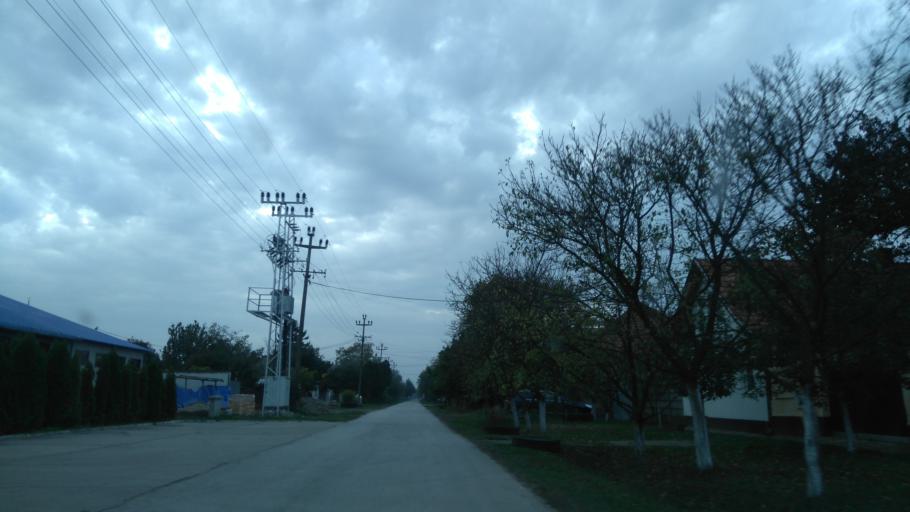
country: RS
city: Mol
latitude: 45.7653
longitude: 20.1349
